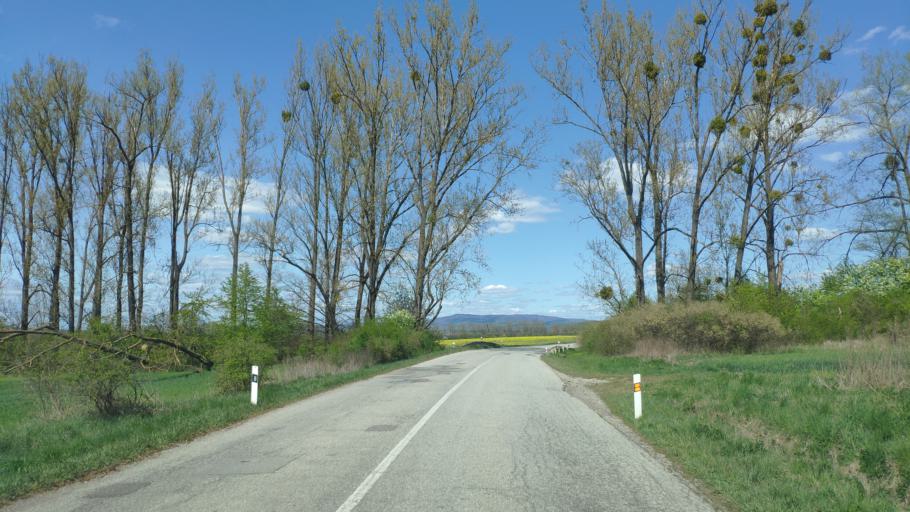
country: SK
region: Kosicky
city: Kosice
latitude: 48.6777
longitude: 21.4208
